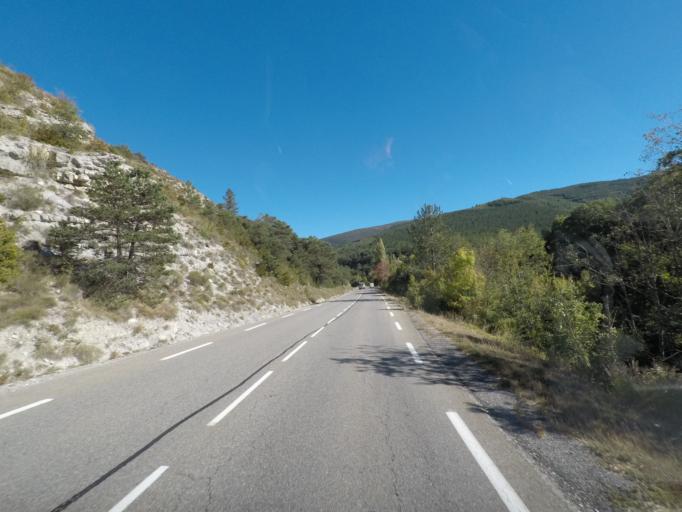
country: FR
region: Provence-Alpes-Cote d'Azur
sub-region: Departement des Hautes-Alpes
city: Serres
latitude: 44.4170
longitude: 5.6578
